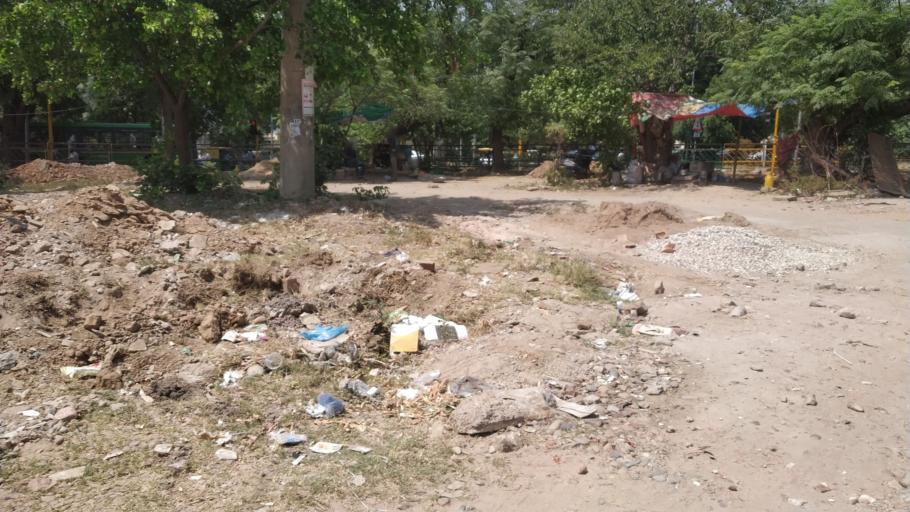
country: IN
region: Punjab
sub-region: Ajitgarh
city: Mohali
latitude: 30.7113
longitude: 76.7290
